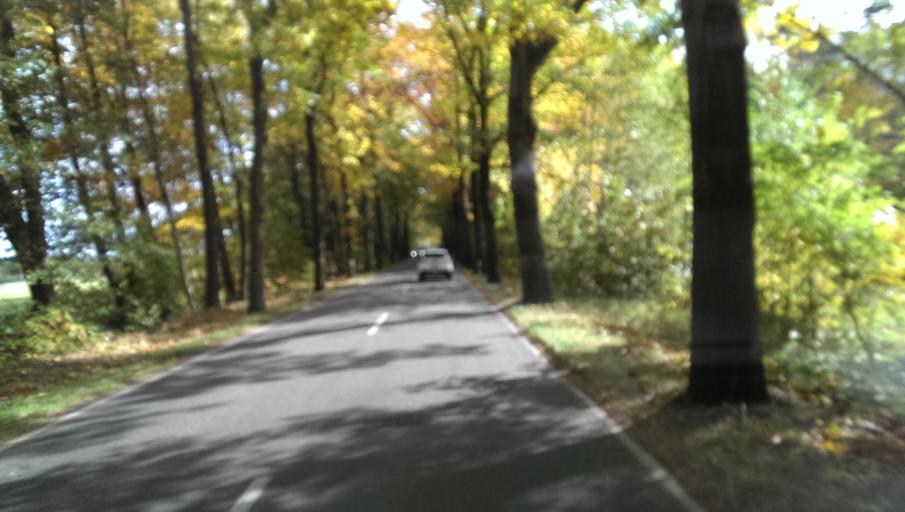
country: DE
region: Saxony
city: Wiednitz
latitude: 51.3849
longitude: 14.0480
